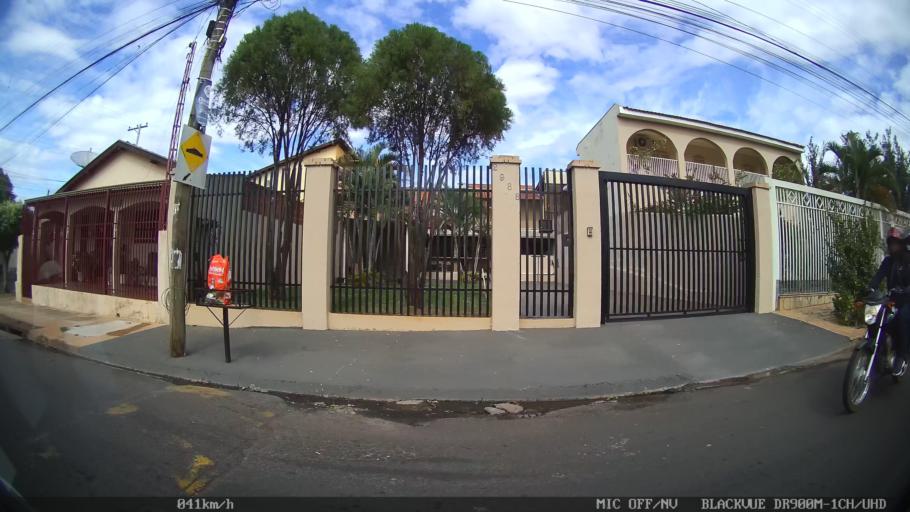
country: BR
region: Sao Paulo
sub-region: Sao Jose Do Rio Preto
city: Sao Jose do Rio Preto
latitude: -20.8072
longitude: -49.5015
